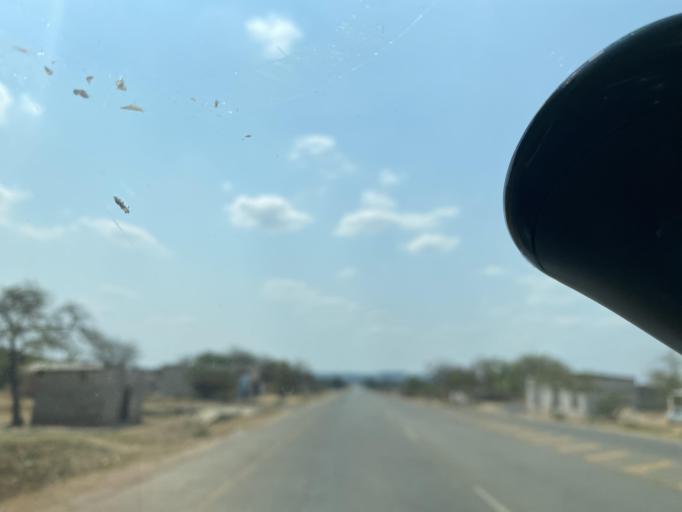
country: ZM
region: Lusaka
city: Chongwe
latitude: -15.5658
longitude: 28.6909
